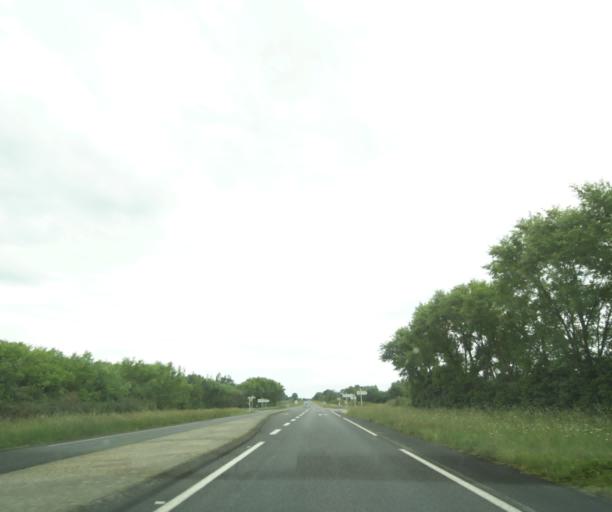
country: FR
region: Poitou-Charentes
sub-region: Departement des Deux-Sevres
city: Airvault
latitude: 46.7973
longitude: -0.2131
